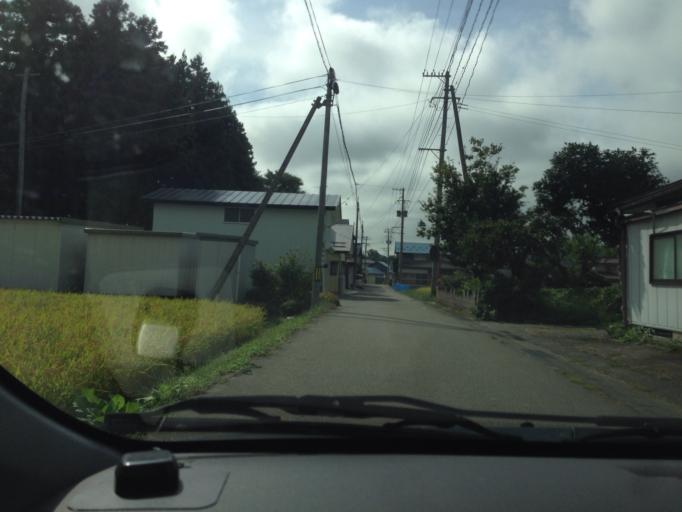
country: JP
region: Fukushima
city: Kitakata
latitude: 37.5205
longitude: 139.8195
